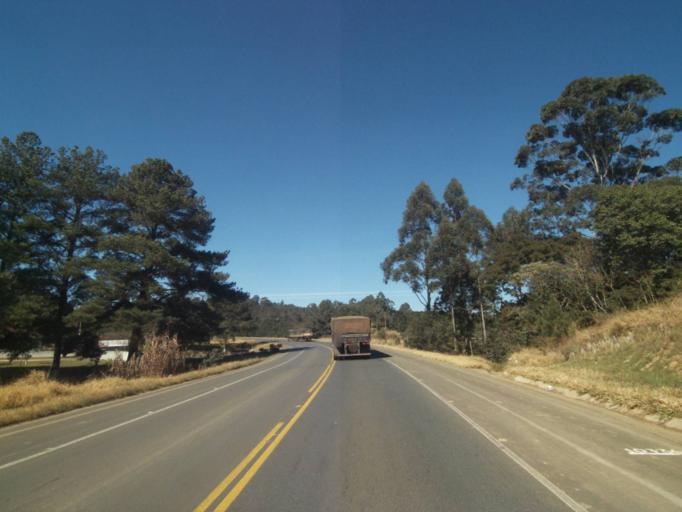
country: BR
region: Parana
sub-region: Tibagi
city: Tibagi
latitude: -24.5772
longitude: -50.4502
